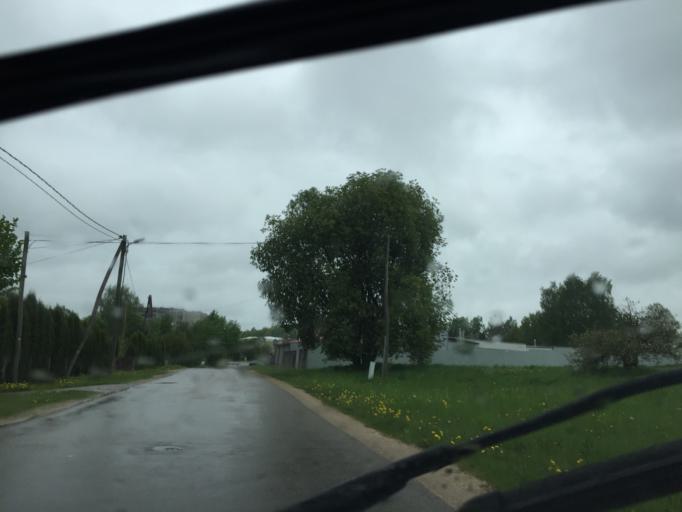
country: LV
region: Lielvarde
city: Lielvarde
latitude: 56.7210
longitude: 24.7973
